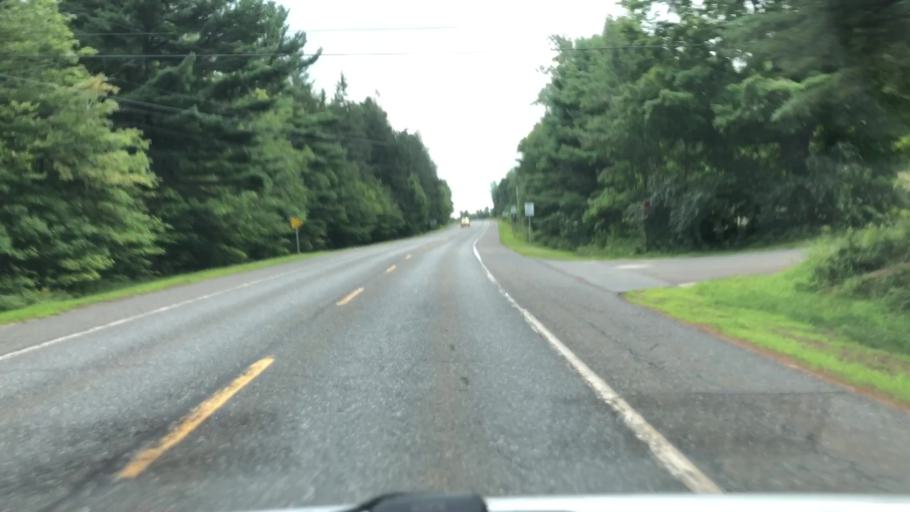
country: US
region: Massachusetts
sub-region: Franklin County
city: Ashfield
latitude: 42.4584
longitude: -72.8051
